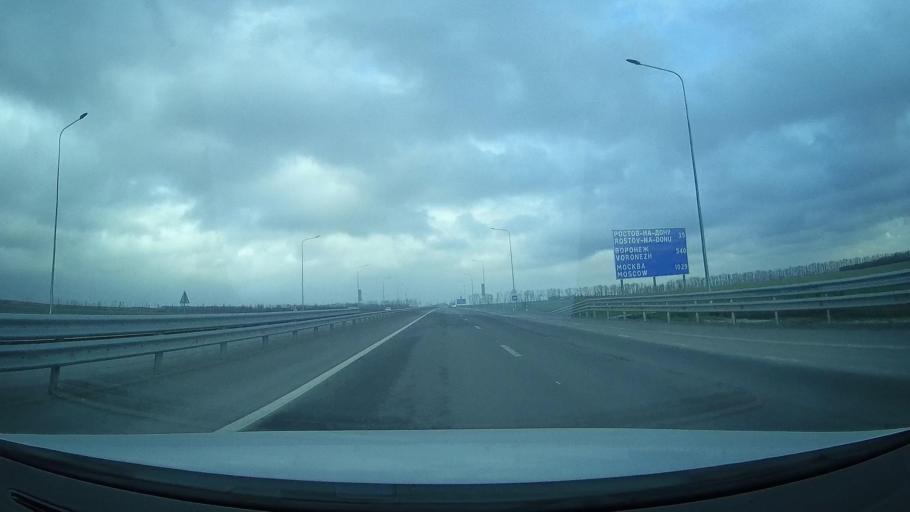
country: RU
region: Rostov
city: Grushevskaya
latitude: 47.4954
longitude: 39.9545
